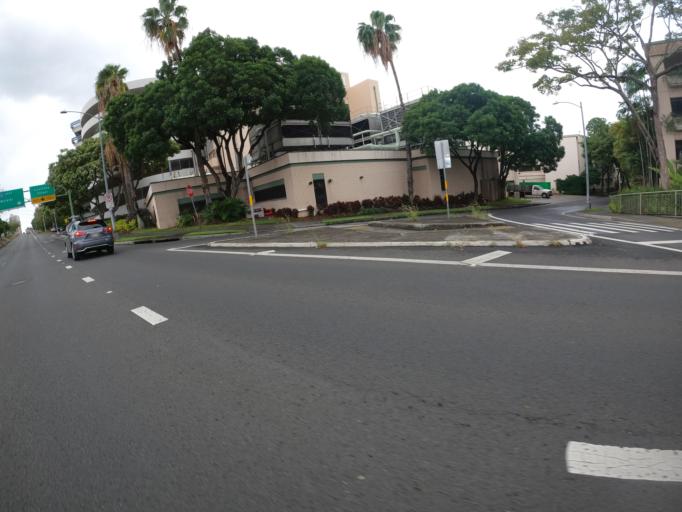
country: US
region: Hawaii
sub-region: Honolulu County
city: Honolulu
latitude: 21.3093
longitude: -157.8535
